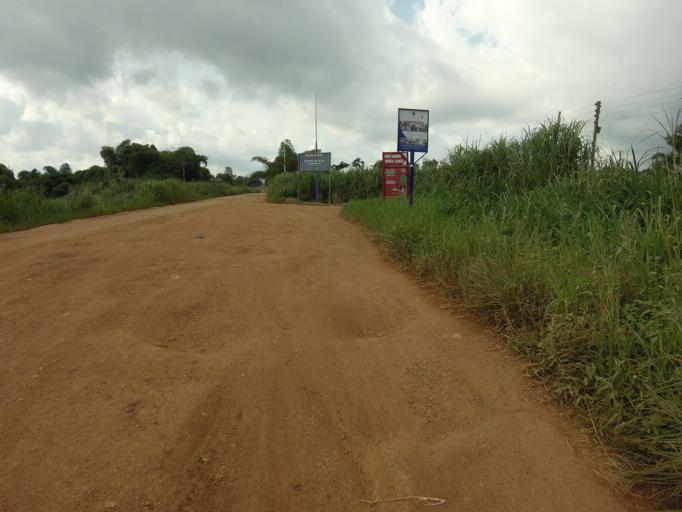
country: GH
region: Volta
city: Hohoe
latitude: 7.1261
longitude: 0.4605
